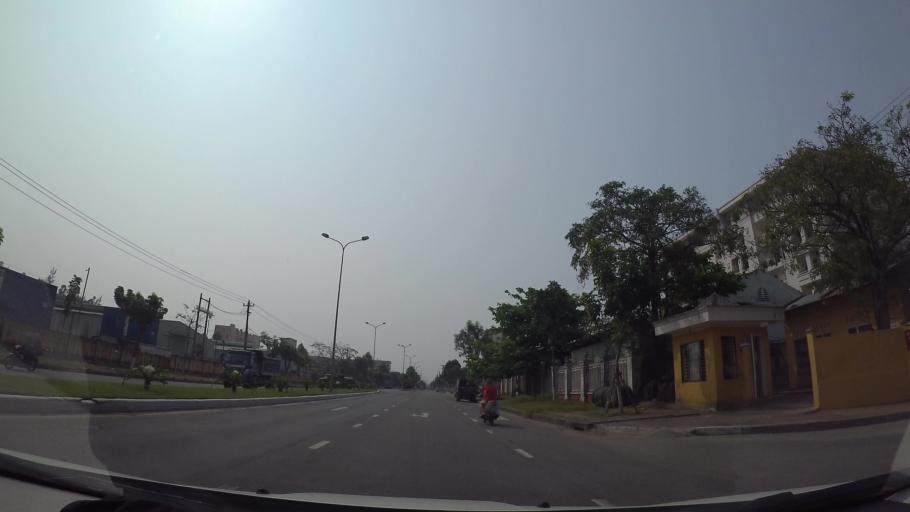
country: VN
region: Da Nang
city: Da Nang
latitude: 16.1104
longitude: 108.2451
